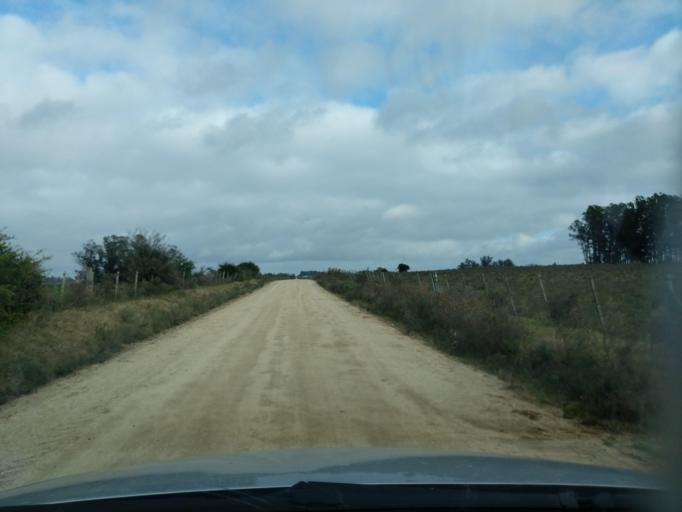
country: UY
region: Florida
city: Florida
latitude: -34.0609
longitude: -56.2061
